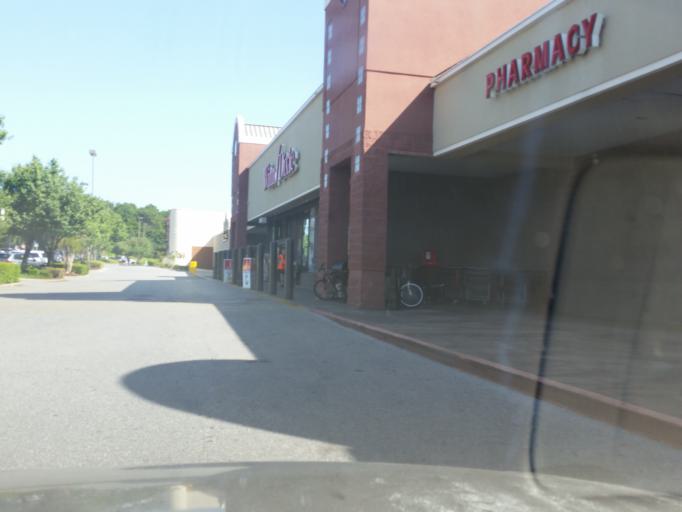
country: US
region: Florida
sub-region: Escambia County
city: Brent
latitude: 30.4700
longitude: -87.2094
